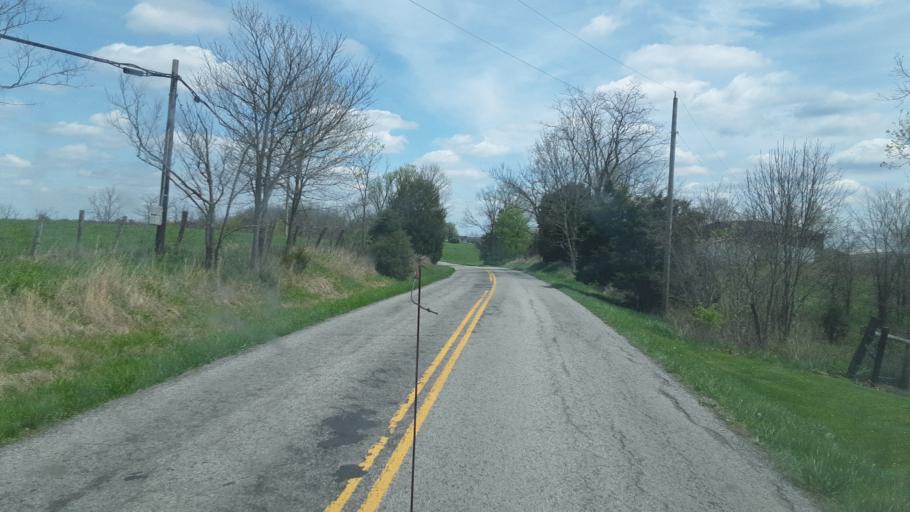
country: US
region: Kentucky
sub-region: Owen County
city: Owenton
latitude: 38.6407
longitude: -84.7619
